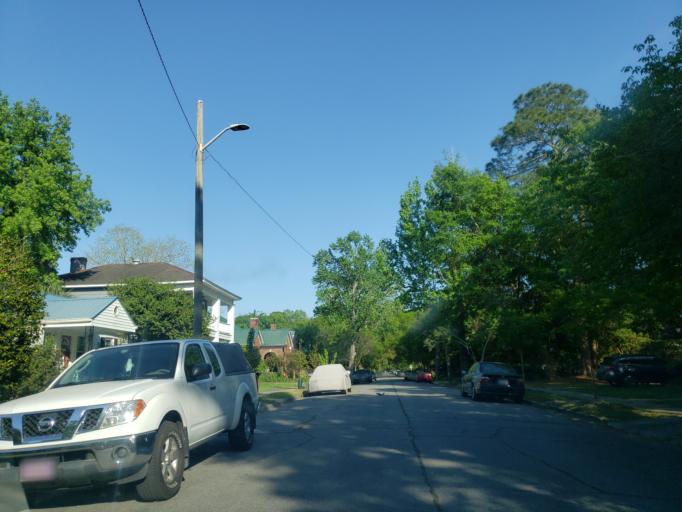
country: US
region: Georgia
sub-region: Chatham County
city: Thunderbolt
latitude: 32.0414
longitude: -81.0850
